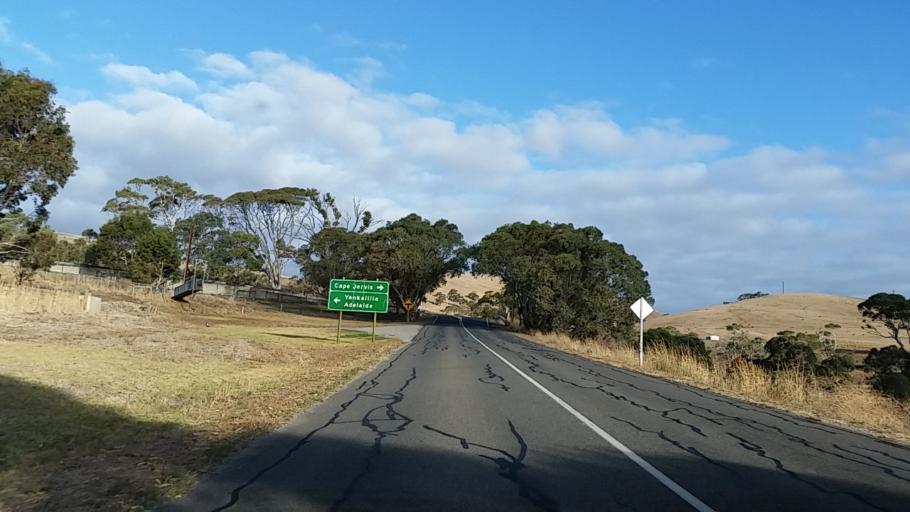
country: AU
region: South Australia
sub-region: Yankalilla
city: Normanville
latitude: -35.5101
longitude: 138.2618
